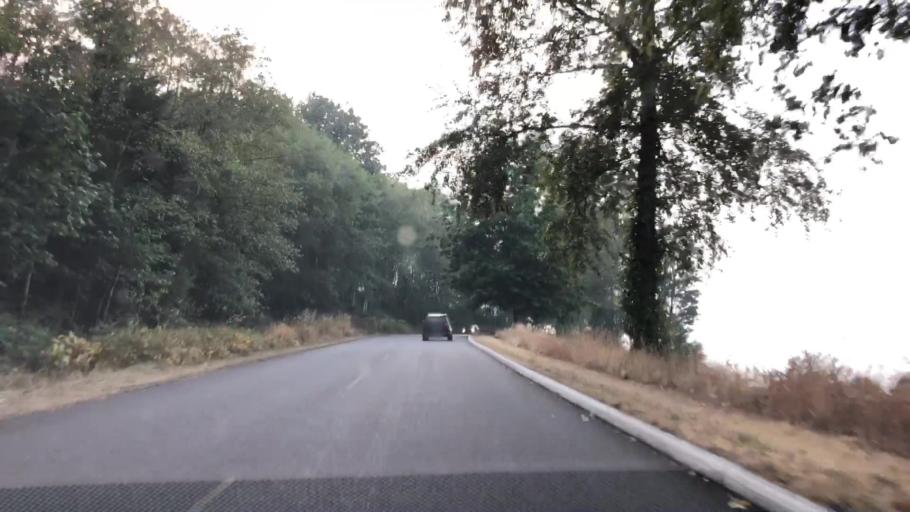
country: US
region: Washington
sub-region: King County
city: Newcastle
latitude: 47.5356
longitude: -122.1346
